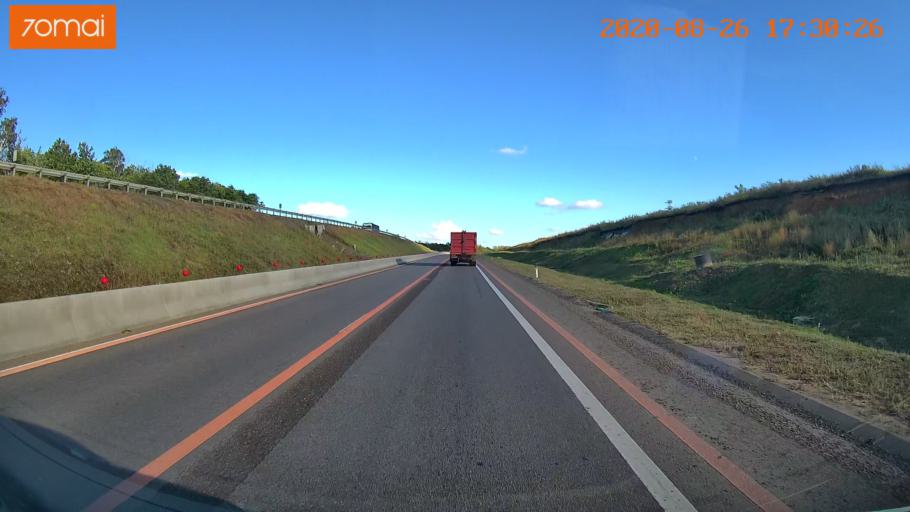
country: RU
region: Tula
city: Kazachka
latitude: 53.4448
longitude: 38.1690
